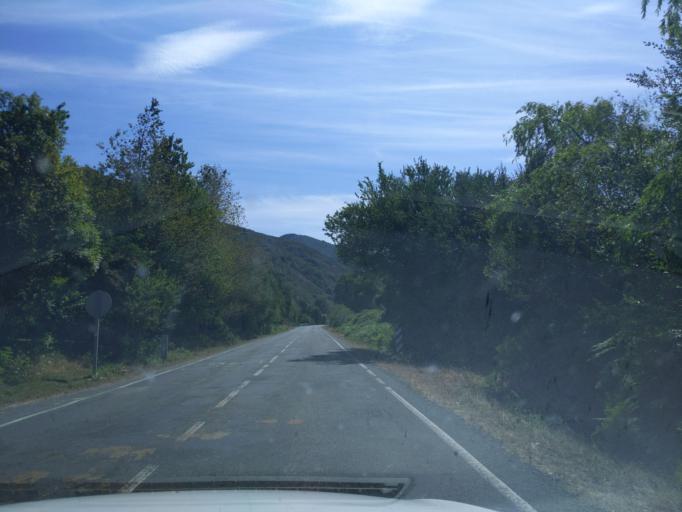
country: ES
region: La Rioja
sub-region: Provincia de La Rioja
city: Ezcaray
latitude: 42.2956
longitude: -3.0251
